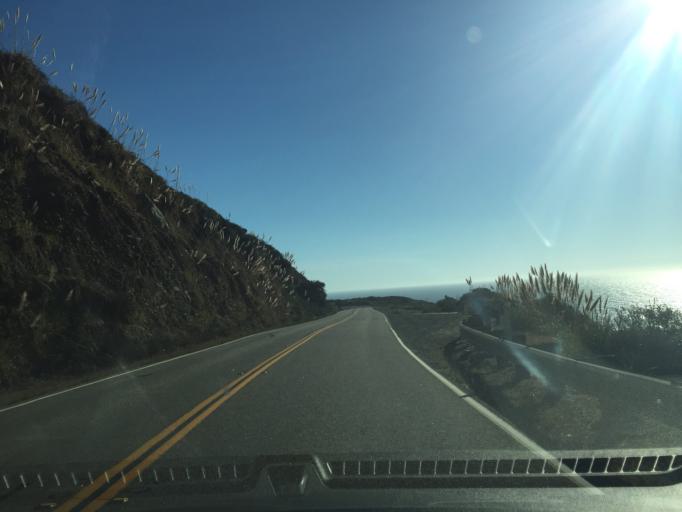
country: US
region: California
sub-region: Monterey County
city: King City
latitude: 35.9030
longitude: -121.4615
